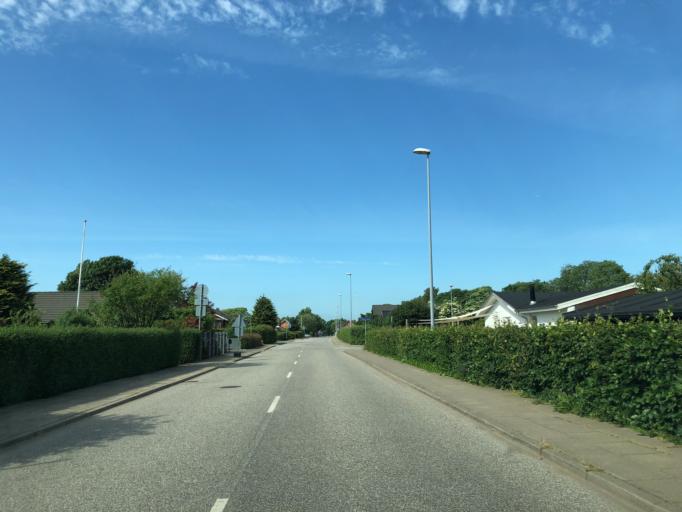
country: DK
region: Central Jutland
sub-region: Herning Kommune
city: Snejbjerg
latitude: 56.1281
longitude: 8.8884
